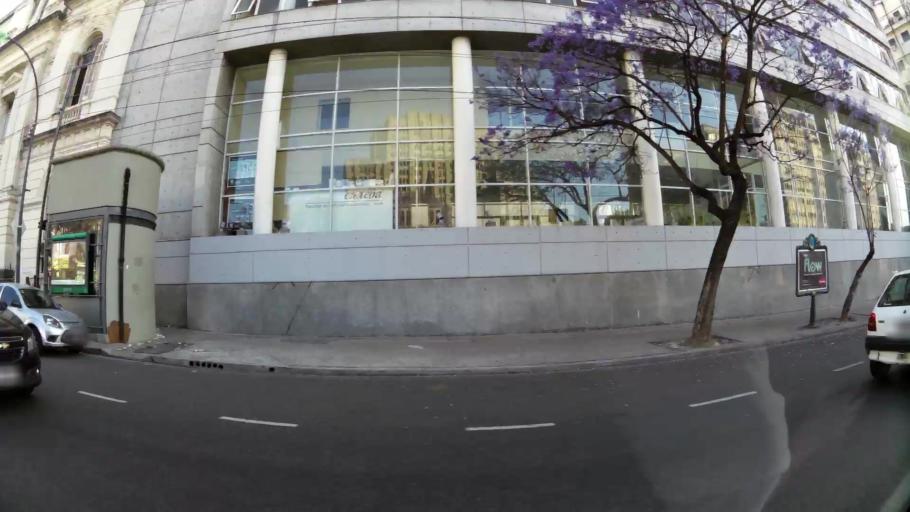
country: AR
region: Buenos Aires F.D.
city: Retiro
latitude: -34.5996
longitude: -58.3983
